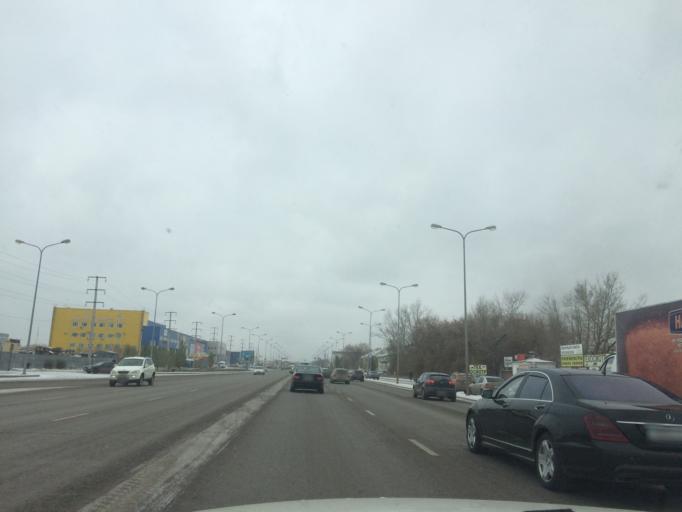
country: KZ
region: Astana Qalasy
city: Astana
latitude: 51.1814
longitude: 71.4610
